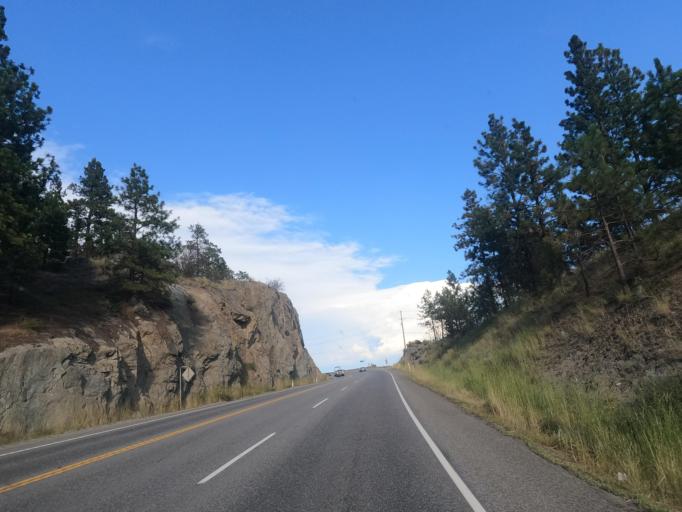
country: CA
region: British Columbia
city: Peachland
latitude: 49.8003
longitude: -119.6756
